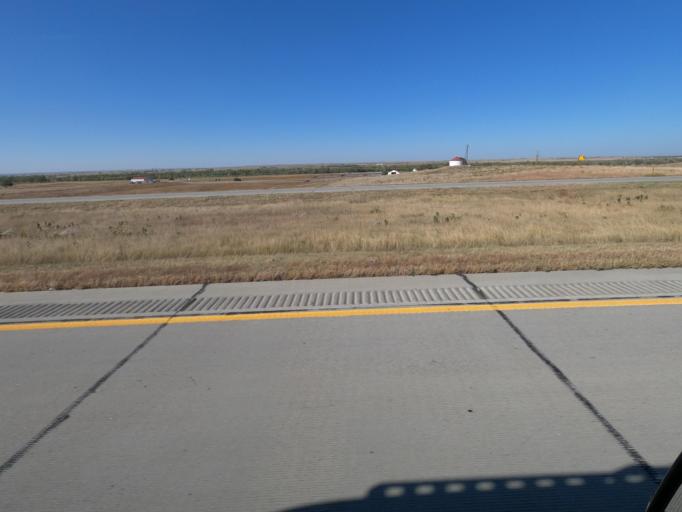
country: US
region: Colorado
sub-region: Sedgwick County
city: Julesburg
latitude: 40.9365
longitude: -102.3052
